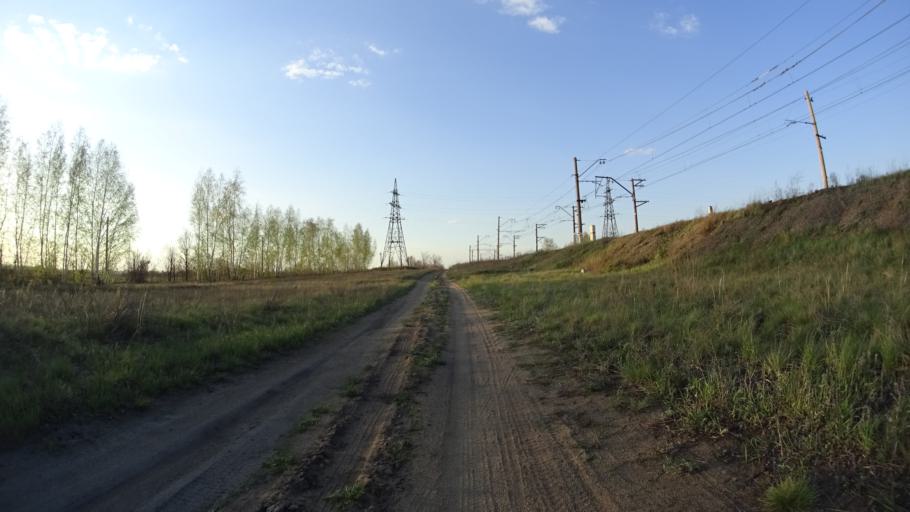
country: RU
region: Chelyabinsk
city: Troitsk
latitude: 54.0599
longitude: 61.6136
